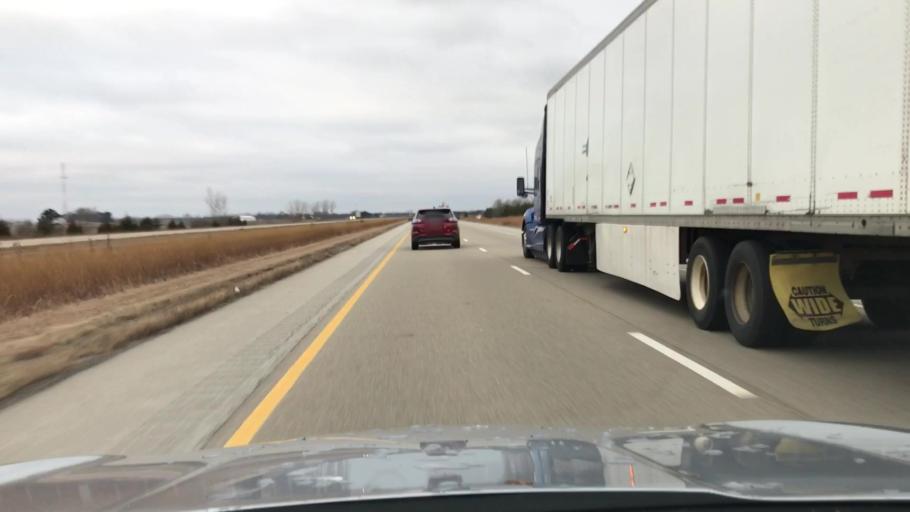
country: US
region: Illinois
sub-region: Logan County
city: Lincoln
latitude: 40.1841
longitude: -89.3321
